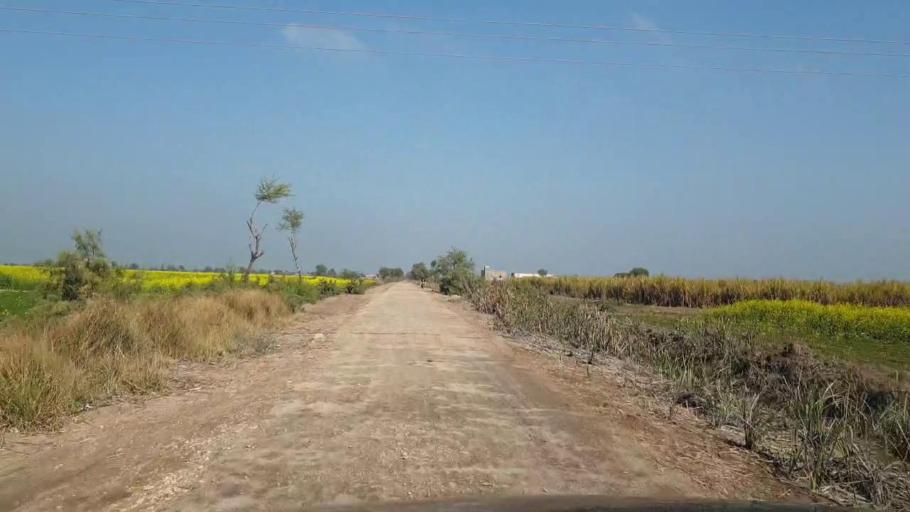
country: PK
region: Sindh
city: Sinjhoro
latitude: 26.0565
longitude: 68.7728
